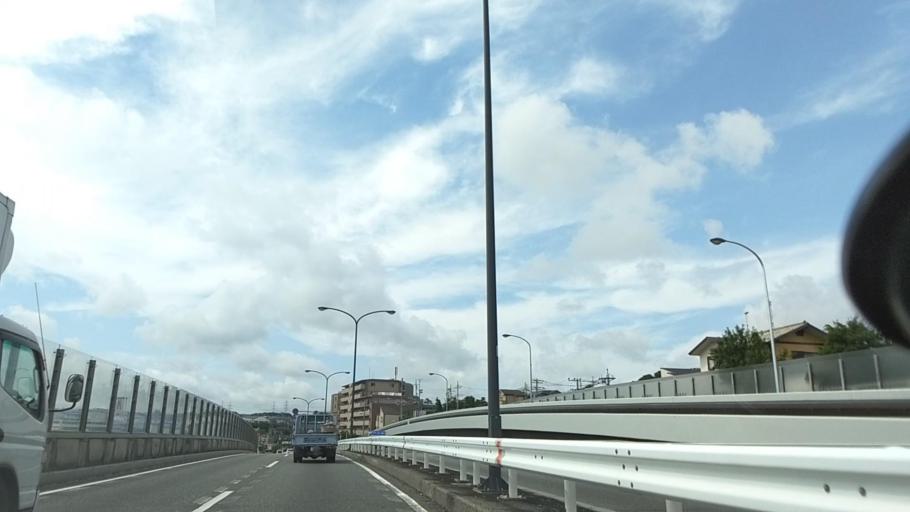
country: JP
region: Kanagawa
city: Yokohama
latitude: 35.4169
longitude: 139.5594
